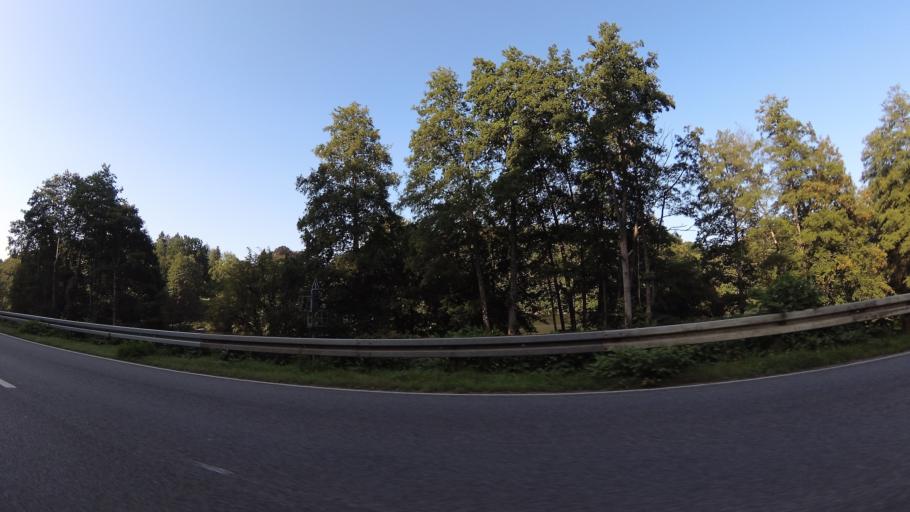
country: DE
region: Saarland
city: Kirkel
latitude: 49.2463
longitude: 7.1865
